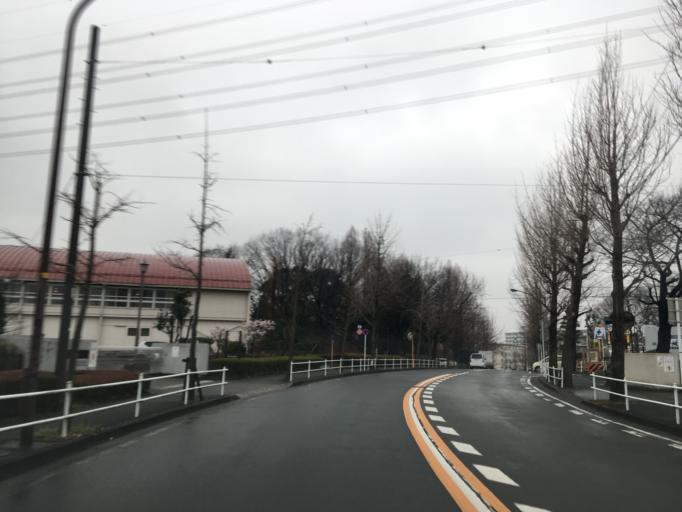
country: JP
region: Tokyo
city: Hino
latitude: 35.6208
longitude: 139.4551
